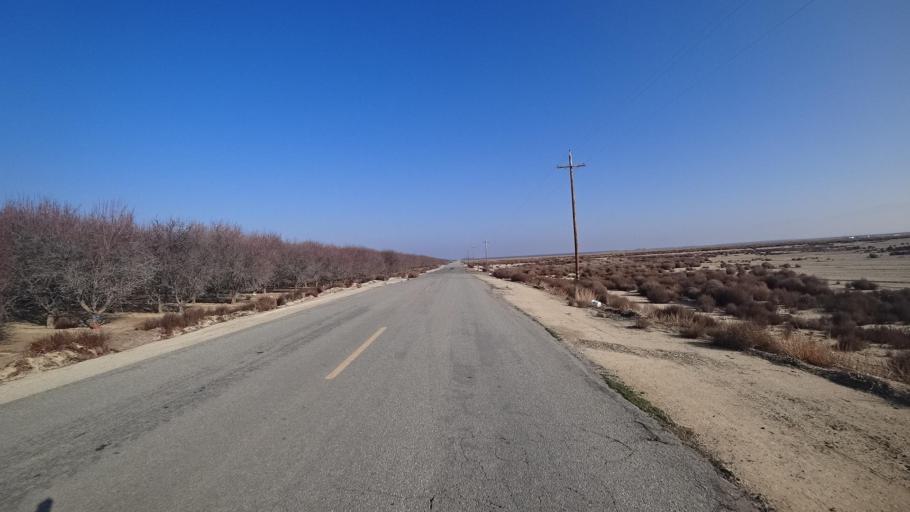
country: US
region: California
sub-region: Kern County
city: Maricopa
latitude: 35.1012
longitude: -119.3549
